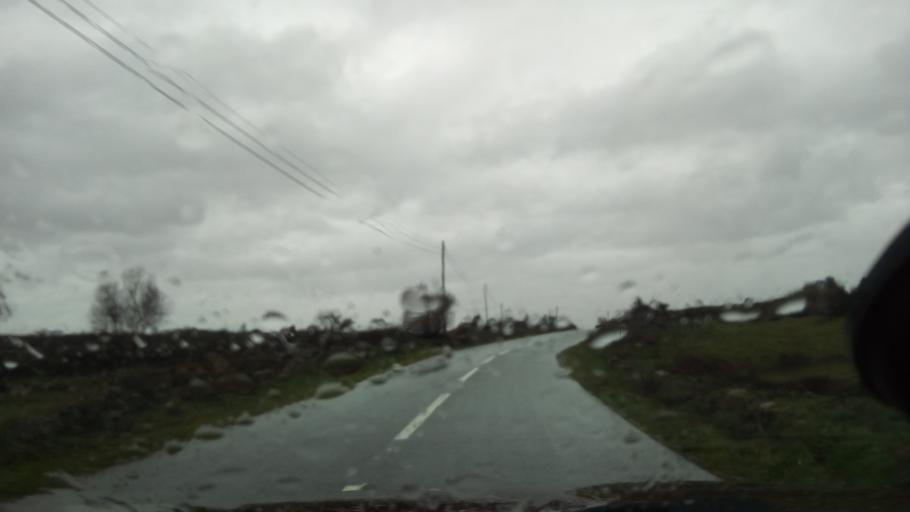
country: PT
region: Guarda
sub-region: Fornos de Algodres
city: Fornos de Algodres
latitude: 40.5627
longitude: -7.5170
